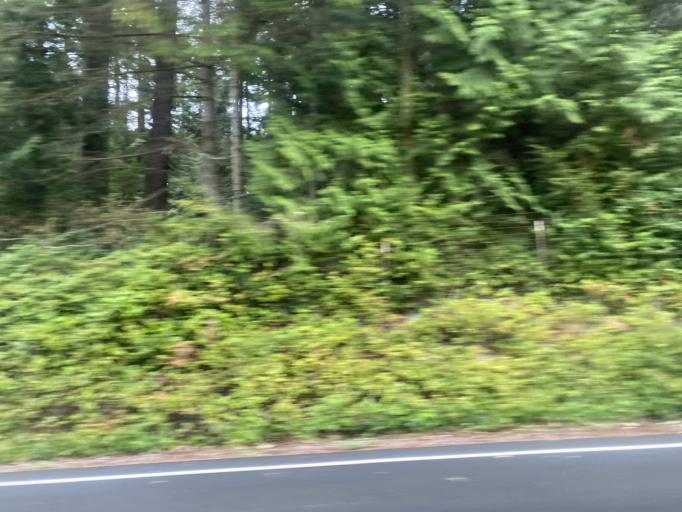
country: US
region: Washington
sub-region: Island County
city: Freeland
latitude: 48.0715
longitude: -122.4851
